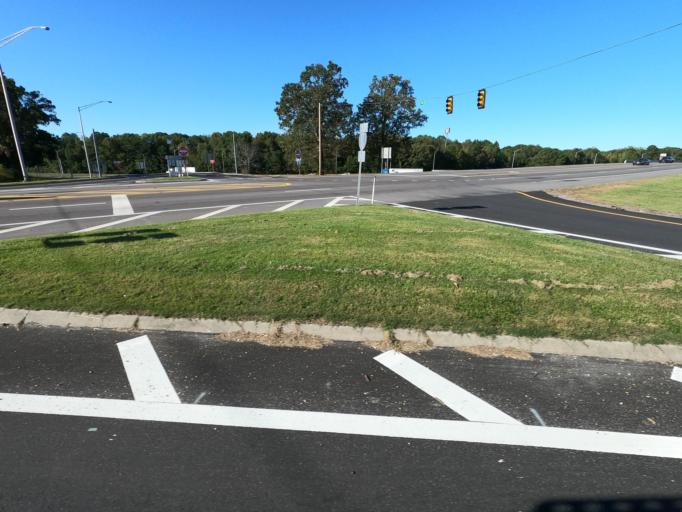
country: US
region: Tennessee
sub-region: Coffee County
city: Manchester
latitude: 35.4570
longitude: -86.0499
